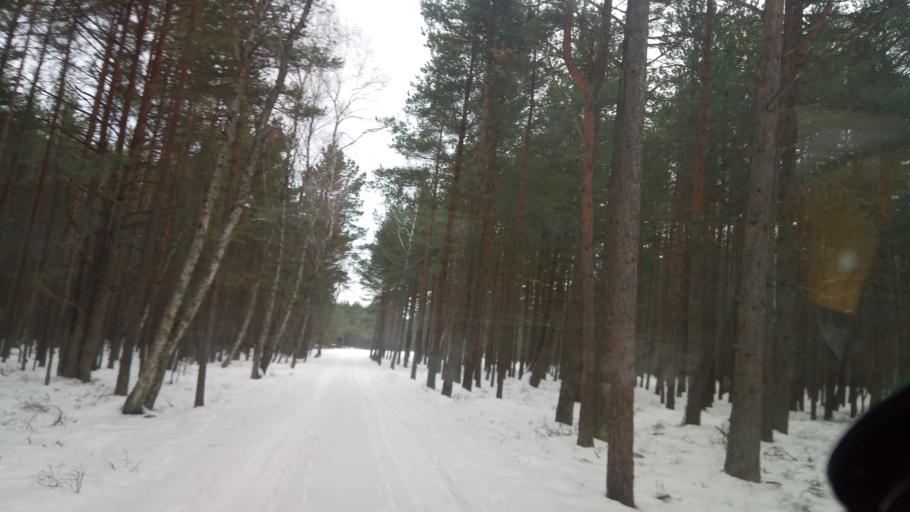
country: LT
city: Neringa
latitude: 55.4225
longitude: 21.0943
